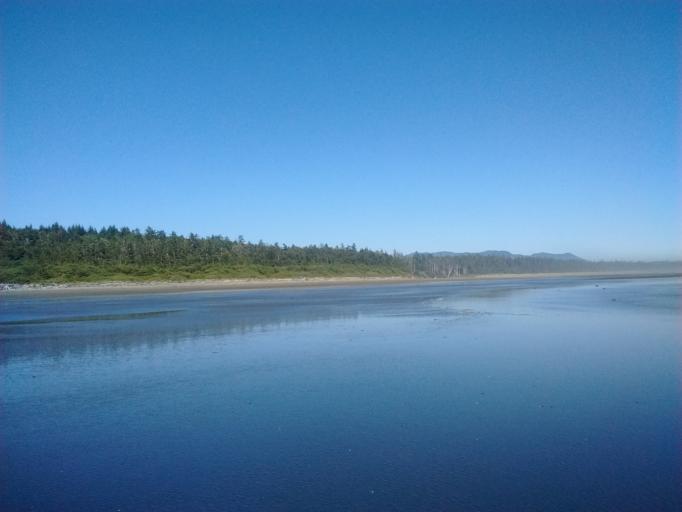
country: CA
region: British Columbia
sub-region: Regional District of Alberni-Clayoquot
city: Ucluelet
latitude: 49.0444
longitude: -125.7137
